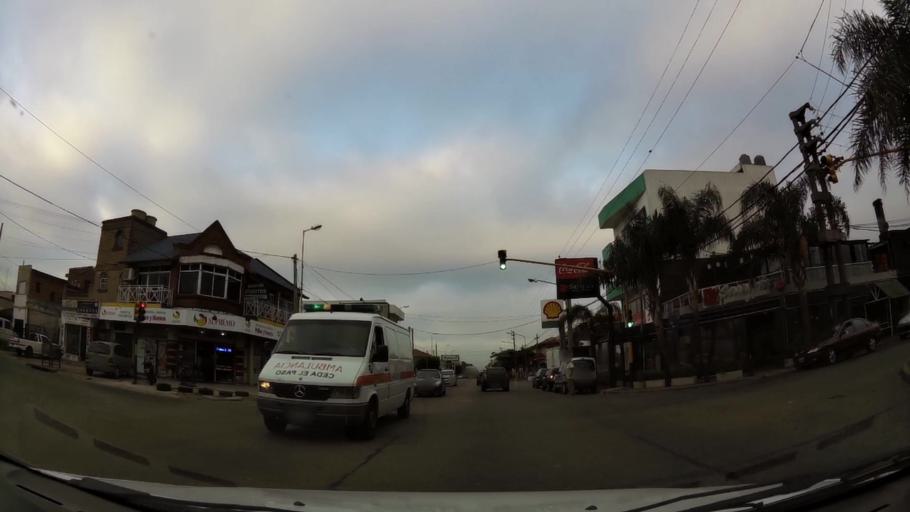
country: AR
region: Buenos Aires
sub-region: Partido de Moron
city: Moron
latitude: -34.6599
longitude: -58.5935
